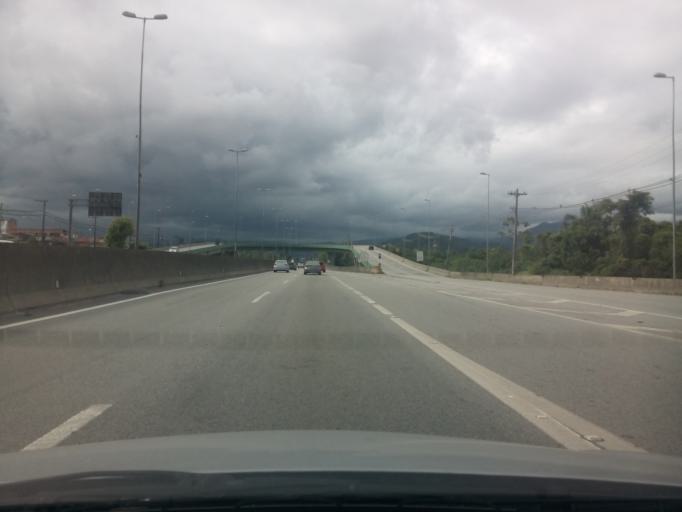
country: BR
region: Sao Paulo
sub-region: Santos
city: Santos
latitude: -23.9383
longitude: -46.2813
